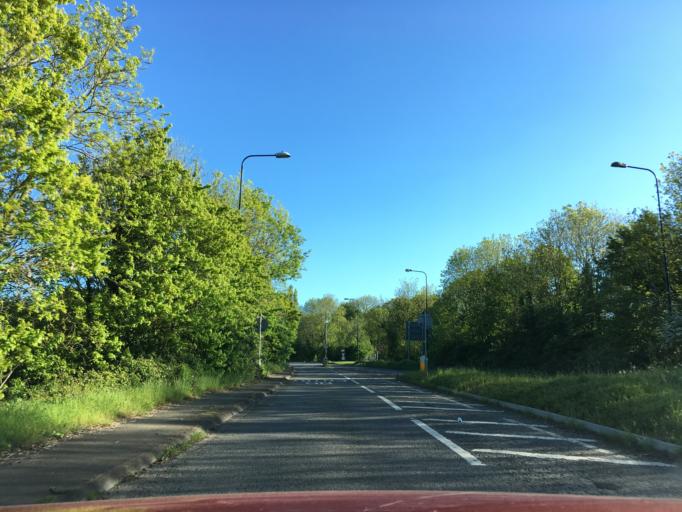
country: GB
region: England
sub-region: North Somerset
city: Long Ashton
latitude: 51.4218
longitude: -2.6898
